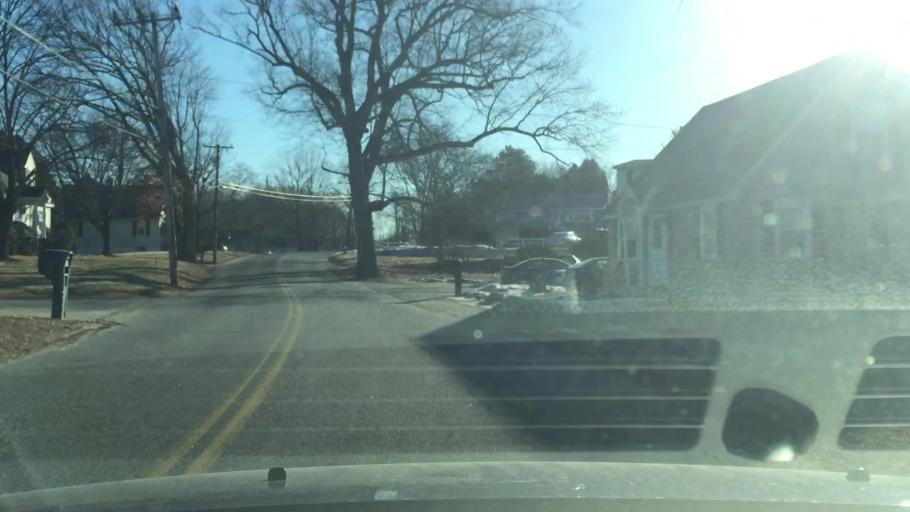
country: US
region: Massachusetts
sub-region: Middlesex County
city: Dracut
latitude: 42.6651
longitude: -71.3373
